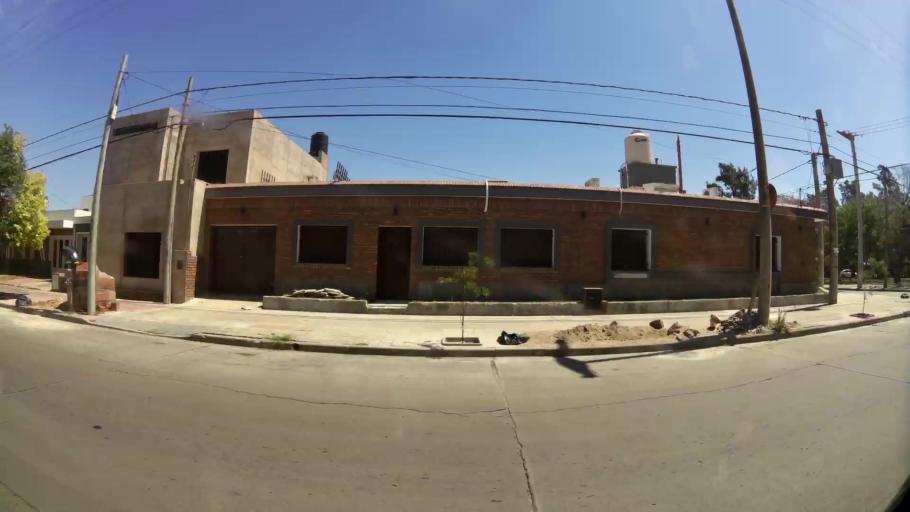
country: AR
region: Cordoba
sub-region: Departamento de Capital
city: Cordoba
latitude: -31.3818
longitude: -64.1634
